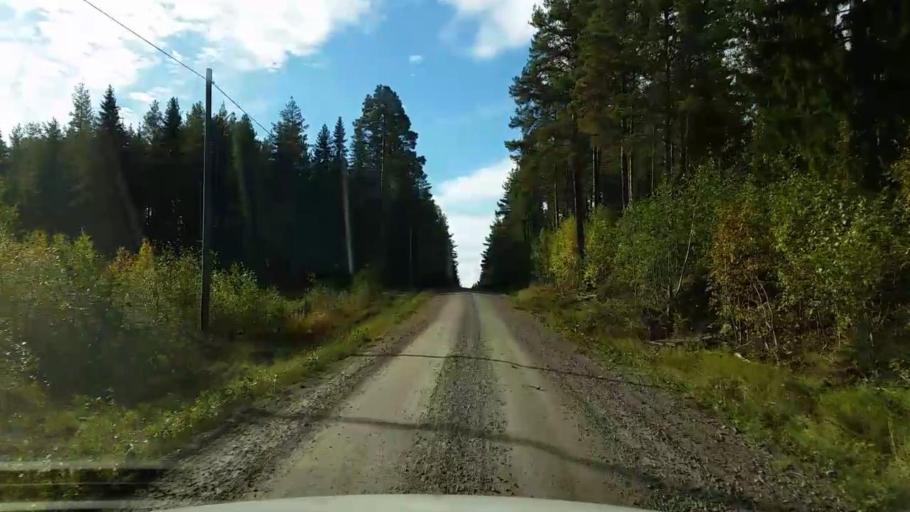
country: SE
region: Gaevleborg
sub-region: Ljusdals Kommun
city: Jaervsoe
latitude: 61.7894
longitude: 16.1717
